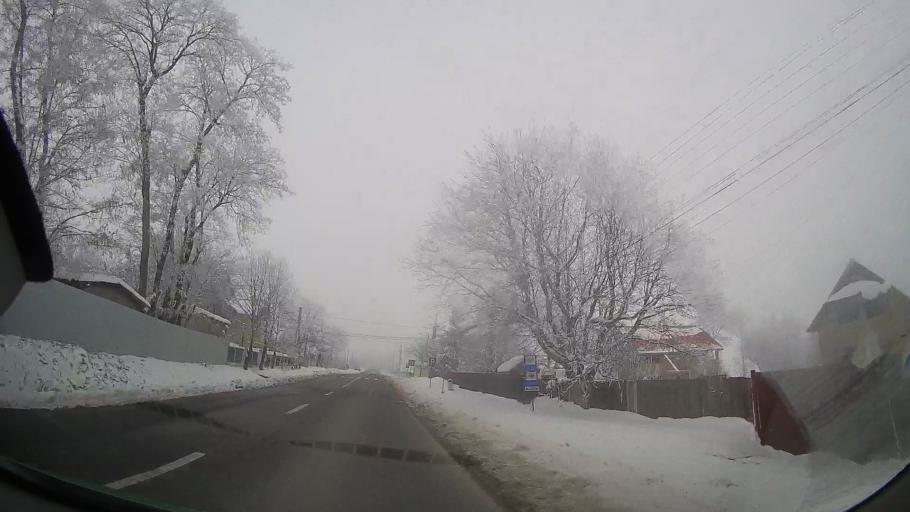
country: RO
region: Iasi
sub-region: Comuna Valea Seaca
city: Valea Seaca
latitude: 47.2941
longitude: 26.6738
